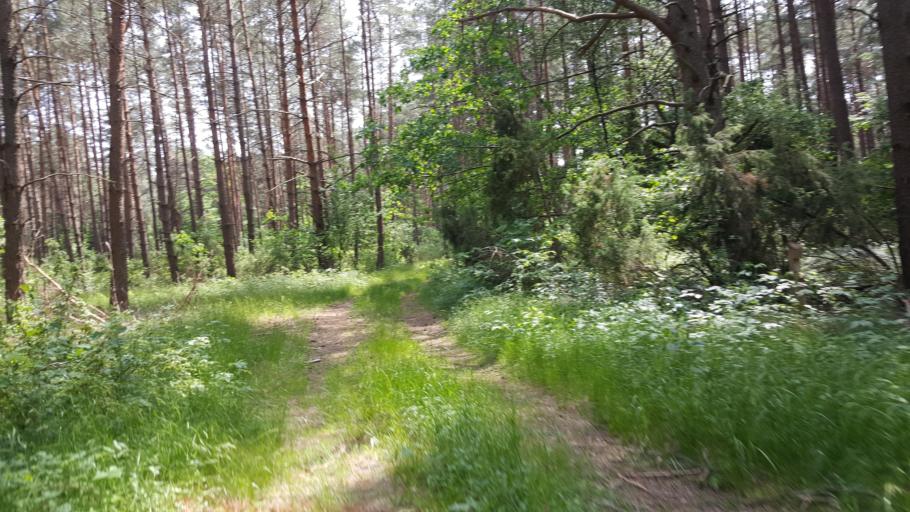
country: BY
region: Brest
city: Kamyanyuki
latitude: 52.5135
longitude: 23.8265
